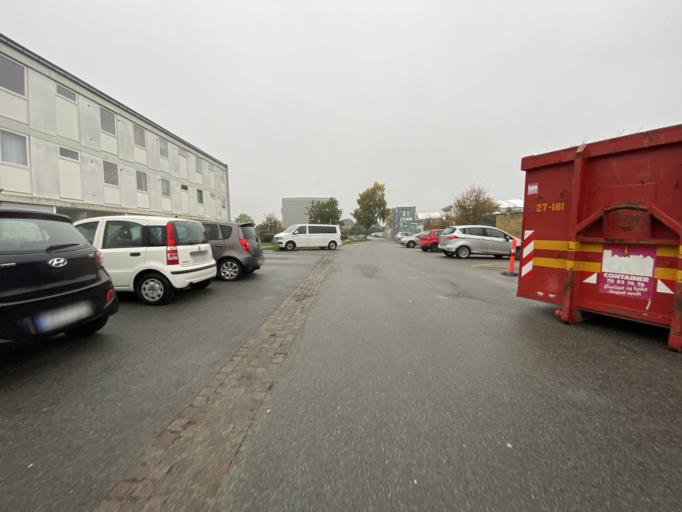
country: DK
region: Capital Region
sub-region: Dragor Kommune
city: Dragor
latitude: 55.5831
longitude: 12.6514
